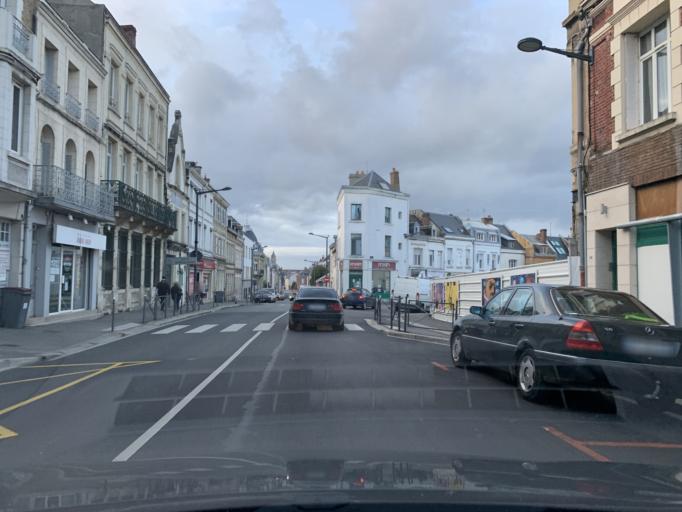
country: FR
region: Picardie
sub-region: Departement de l'Aisne
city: Saint-Quentin
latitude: 49.8497
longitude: 3.2867
